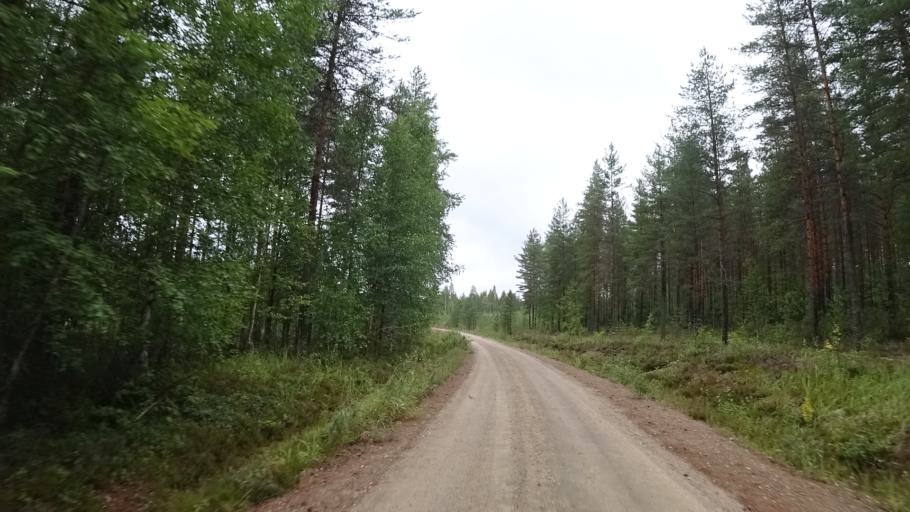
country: FI
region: North Karelia
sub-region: Pielisen Karjala
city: Lieksa
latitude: 63.5169
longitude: 30.1165
